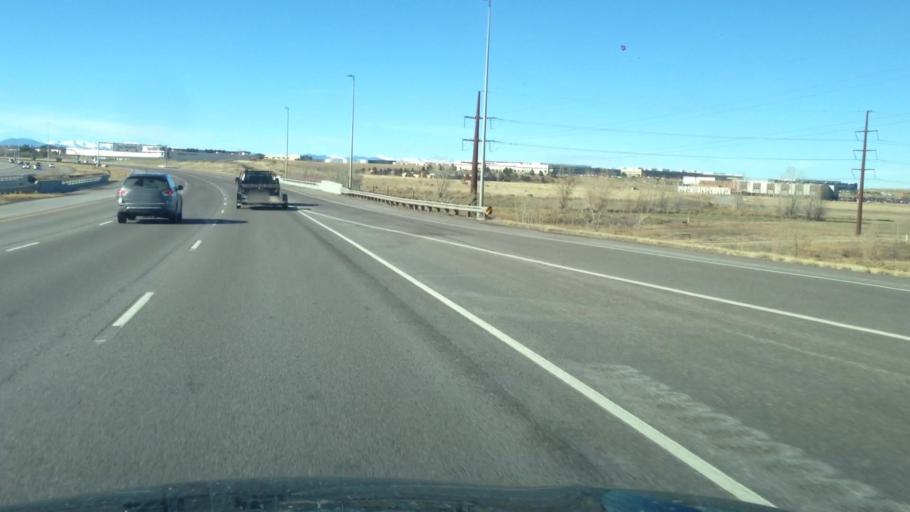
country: US
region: Colorado
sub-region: Douglas County
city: Stonegate
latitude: 39.5545
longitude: -104.8107
